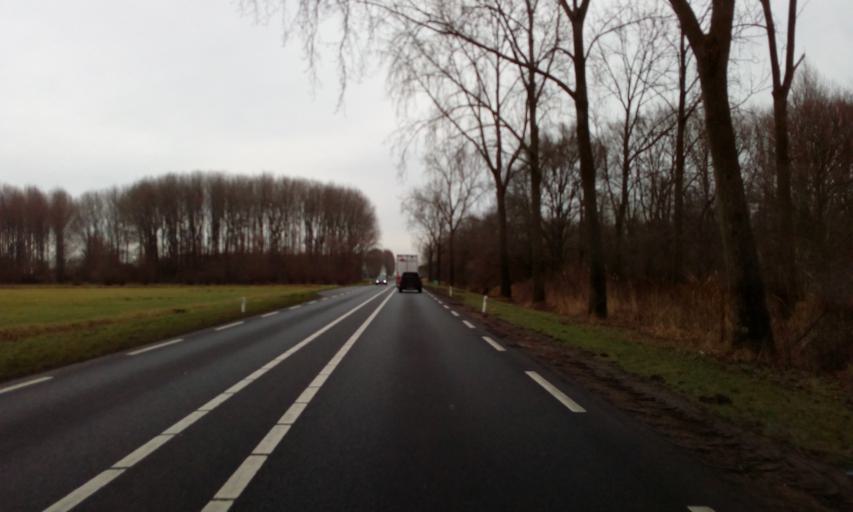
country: NL
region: Gelderland
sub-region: Gemeente Zaltbommel
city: Nederhemert
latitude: 51.7931
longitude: 5.1818
